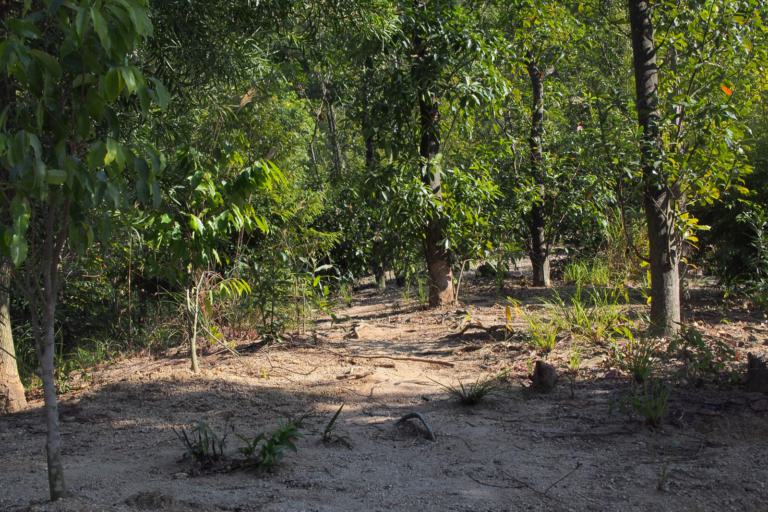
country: CN
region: Guangdong
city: Huancheng
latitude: 22.4554
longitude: 113.4077
